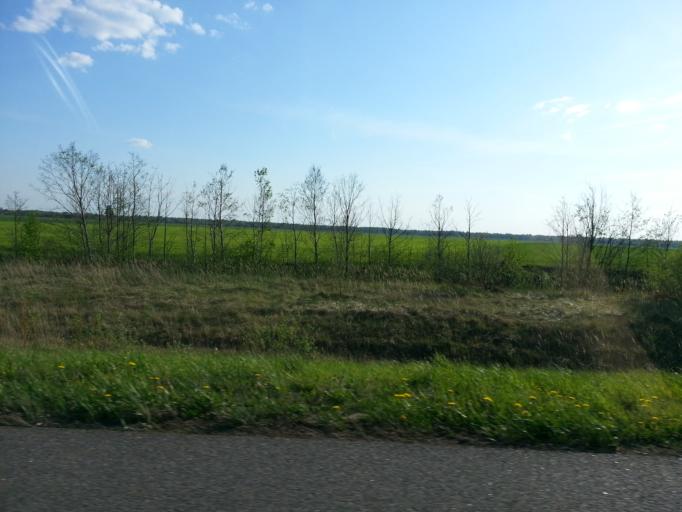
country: LT
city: Ramygala
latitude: 55.5366
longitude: 24.5425
